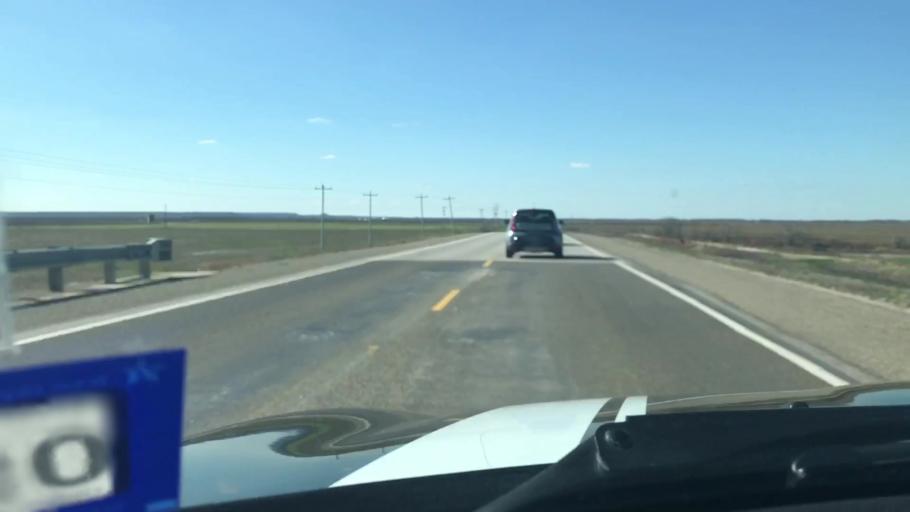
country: US
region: Texas
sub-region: Robertson County
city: Hearne
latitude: 30.8791
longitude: -96.6418
